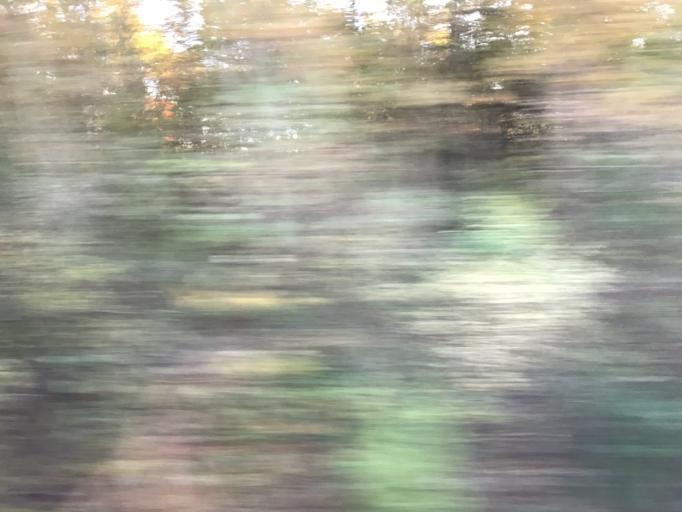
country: DK
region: Capital Region
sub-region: Hvidovre Kommune
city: Hvidovre
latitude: 55.6261
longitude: 12.4588
